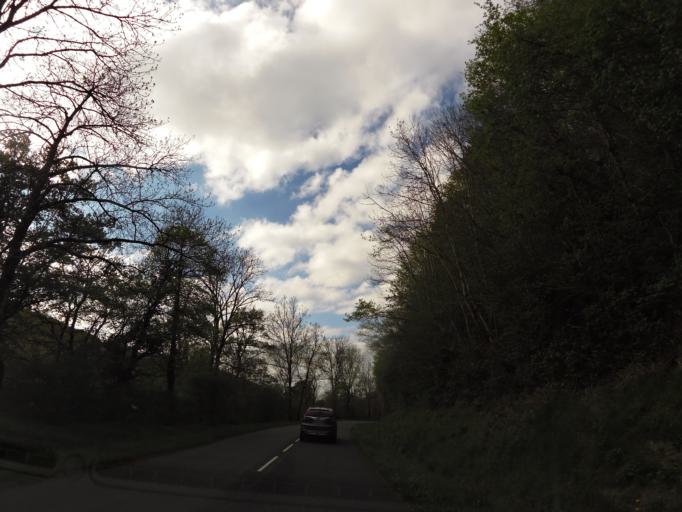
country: FR
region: Midi-Pyrenees
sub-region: Departement du Tarn
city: Soreze
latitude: 43.4239
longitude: 2.0574
